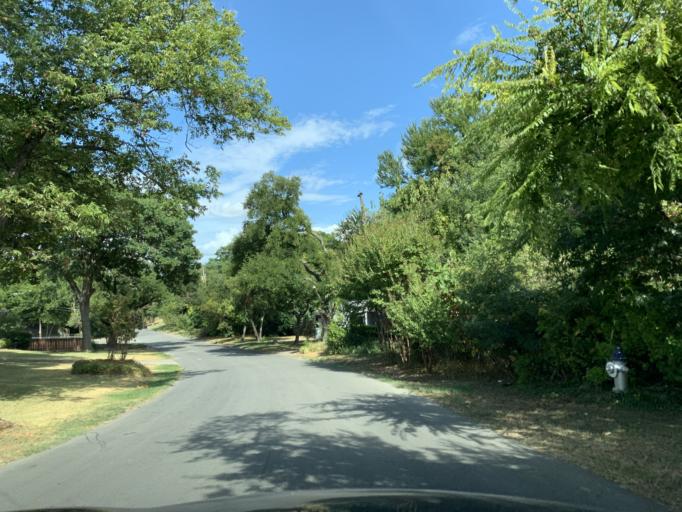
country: US
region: Texas
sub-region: Dallas County
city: Cockrell Hill
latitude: 32.7462
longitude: -96.8682
